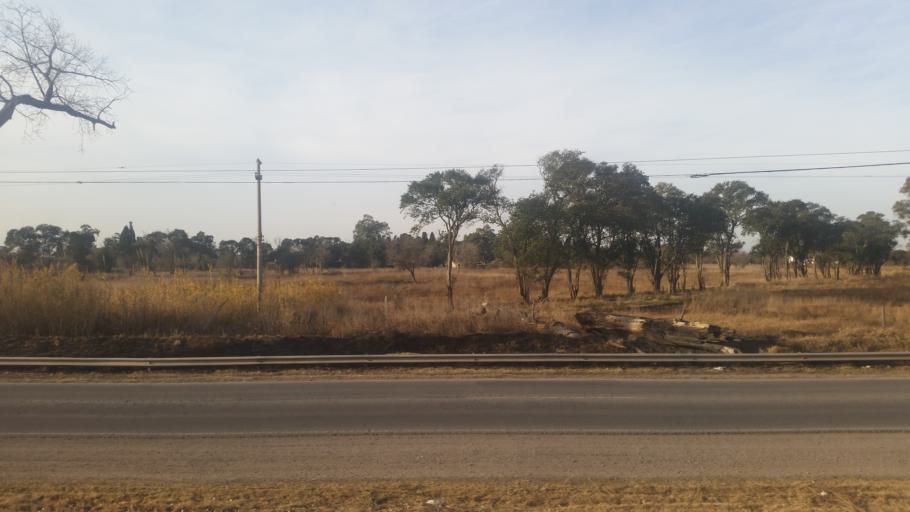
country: AR
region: Cordoba
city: Malvinas Argentinas
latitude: -31.4711
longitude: -64.0969
